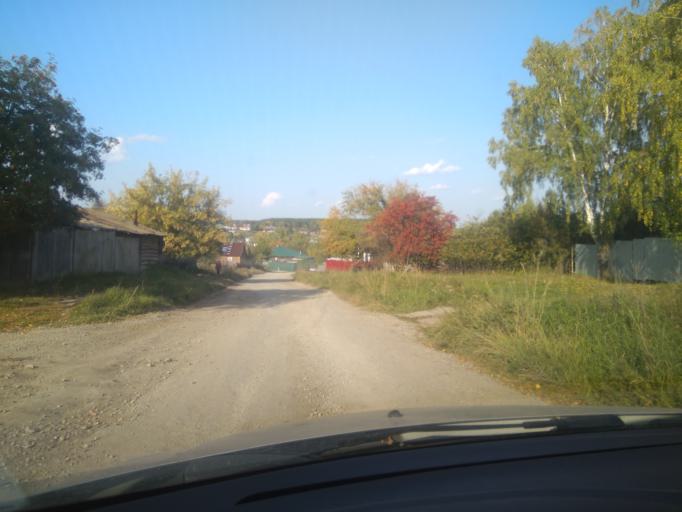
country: RU
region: Sverdlovsk
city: Pokrovskoye
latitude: 56.4319
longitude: 61.5935
